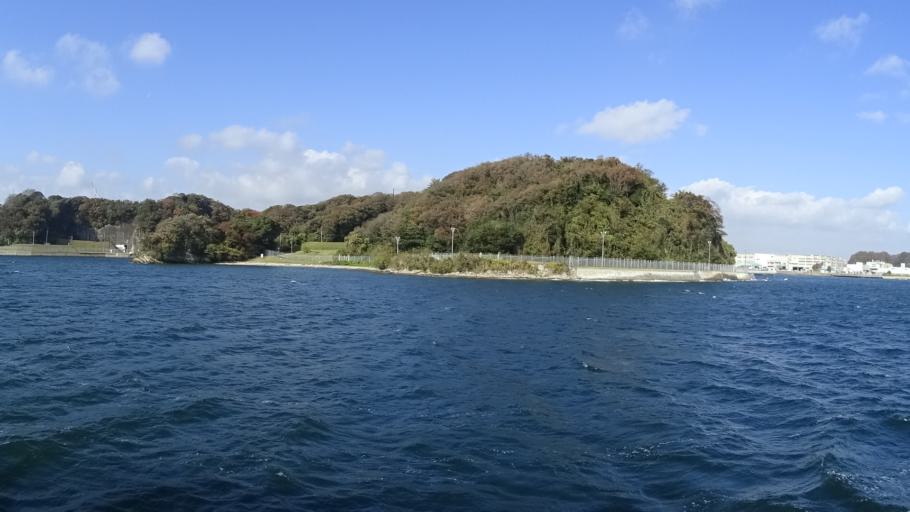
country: JP
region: Kanagawa
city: Yokosuka
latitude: 35.3024
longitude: 139.6431
